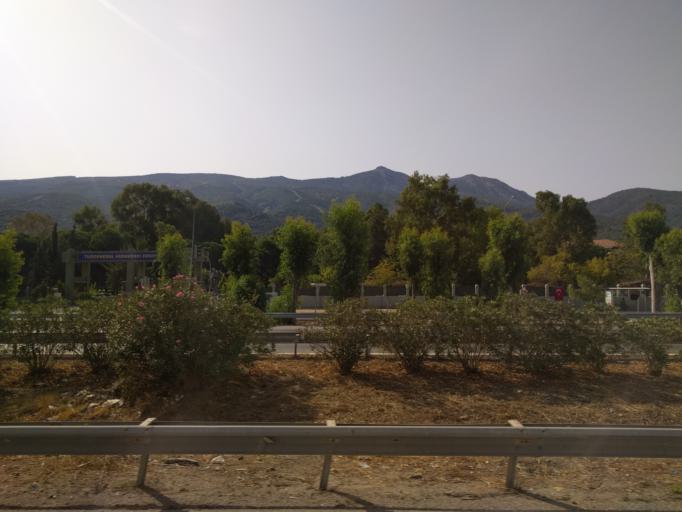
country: TR
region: Izmir
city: Karsiyaka
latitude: 38.3931
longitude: 26.9643
